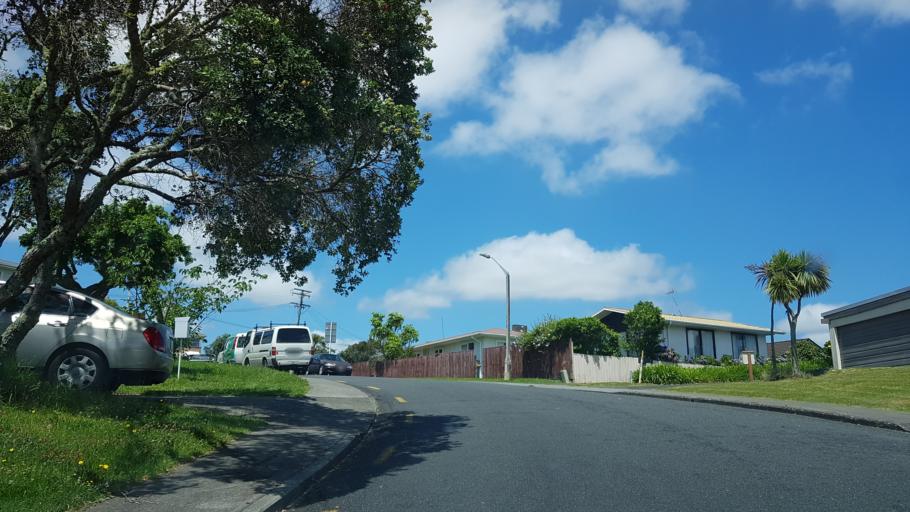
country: NZ
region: Auckland
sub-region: Auckland
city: North Shore
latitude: -36.7887
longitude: 174.7130
